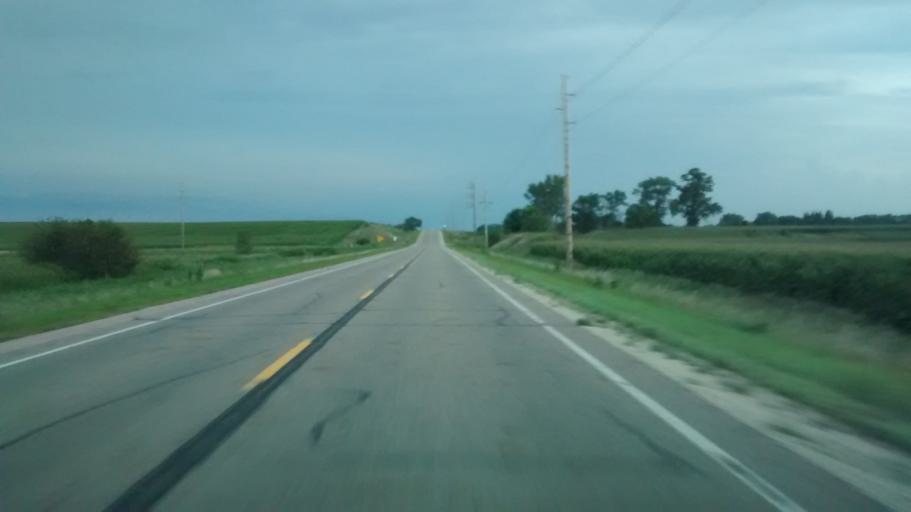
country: US
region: Iowa
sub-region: Woodbury County
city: Moville
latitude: 42.5204
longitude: -96.0463
